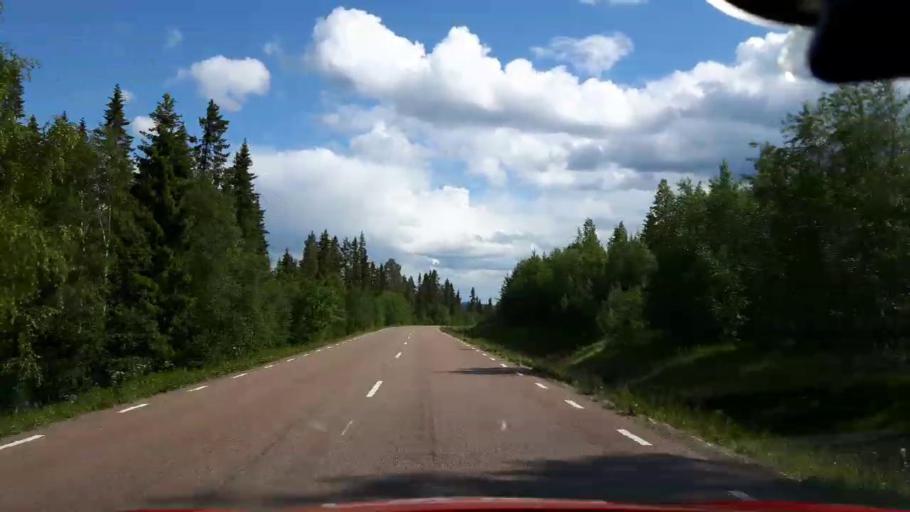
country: SE
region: Jaemtland
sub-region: Krokoms Kommun
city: Valla
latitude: 63.9945
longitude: 14.2349
